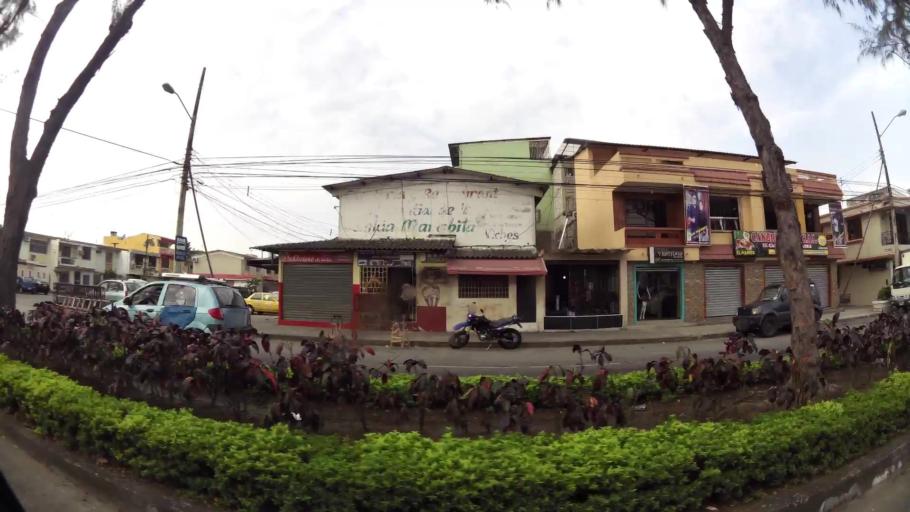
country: EC
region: Guayas
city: Eloy Alfaro
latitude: -2.1371
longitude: -79.8926
